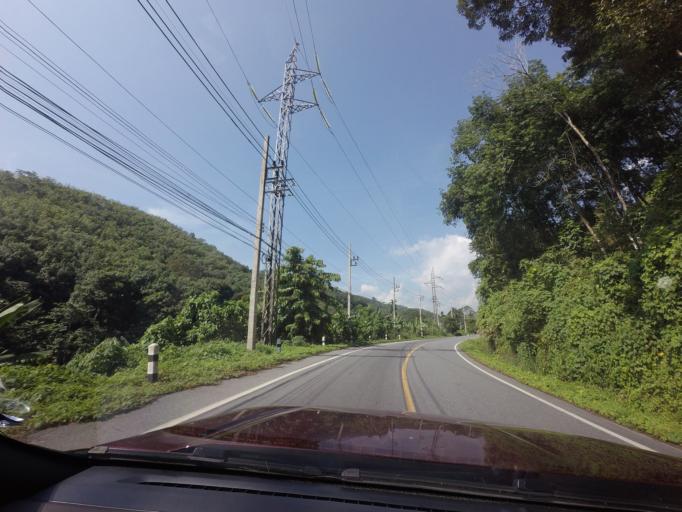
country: TH
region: Yala
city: Than To
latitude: 5.9533
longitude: 101.1941
